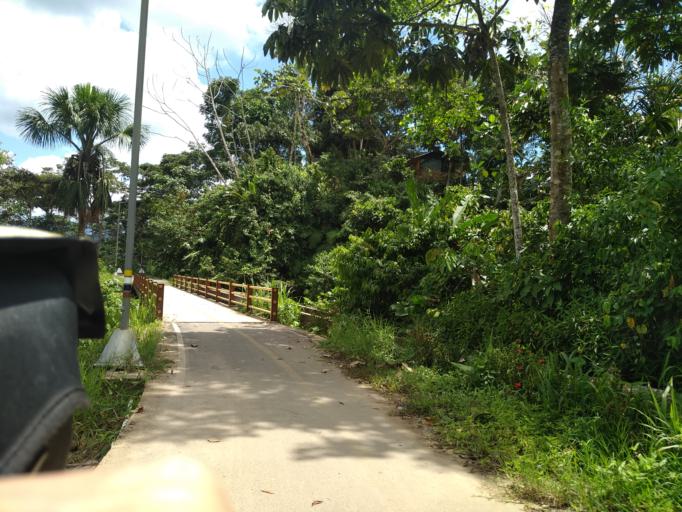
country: EC
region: Napo
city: Tena
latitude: -0.9890
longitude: -77.8229
